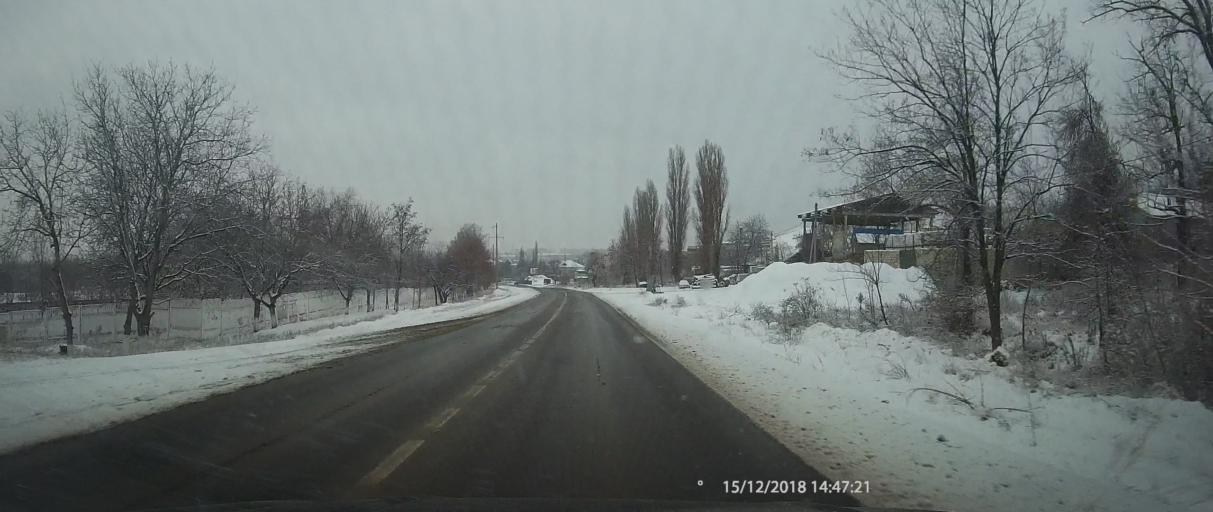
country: MD
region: Cahul
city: Cahul
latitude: 45.8927
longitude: 28.2071
